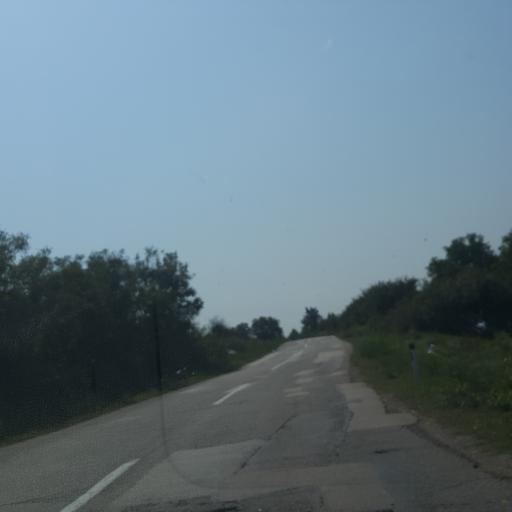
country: RS
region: Central Serbia
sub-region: Zajecarski Okrug
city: Zajecar
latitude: 43.7409
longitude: 22.3119
